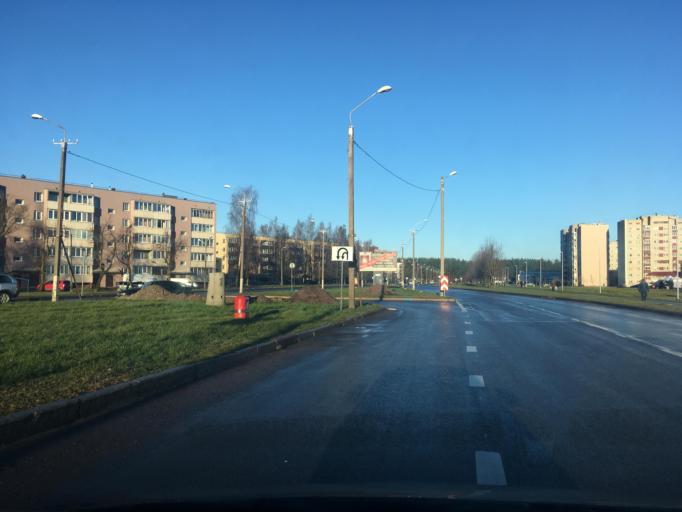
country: EE
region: Ida-Virumaa
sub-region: Narva linn
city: Narva
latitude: 59.3874
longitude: 28.1754
